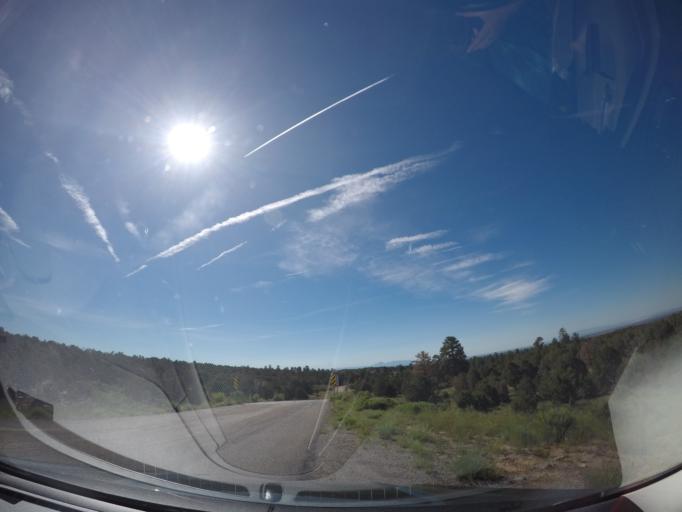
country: US
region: Utah
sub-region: San Juan County
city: Blanding
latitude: 37.7306
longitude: -109.4107
